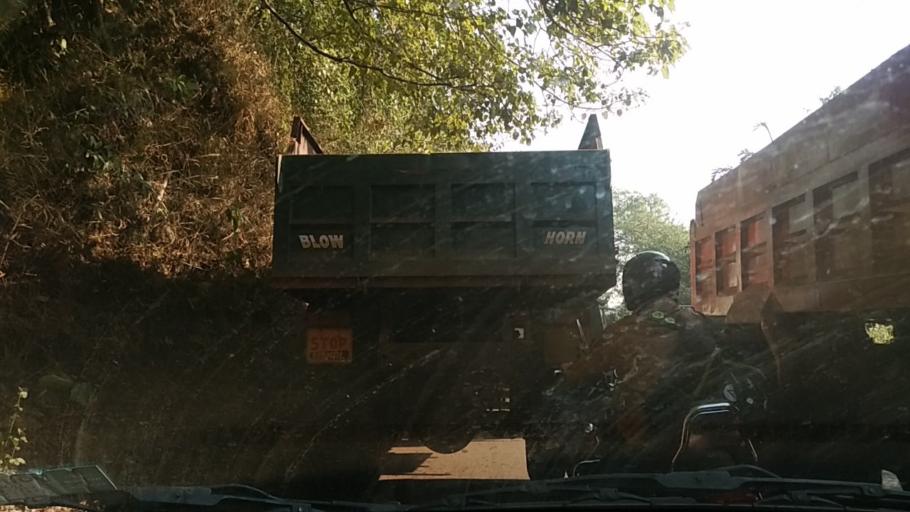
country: IN
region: Goa
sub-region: South Goa
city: Sanvordem
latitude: 15.2696
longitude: 74.1163
